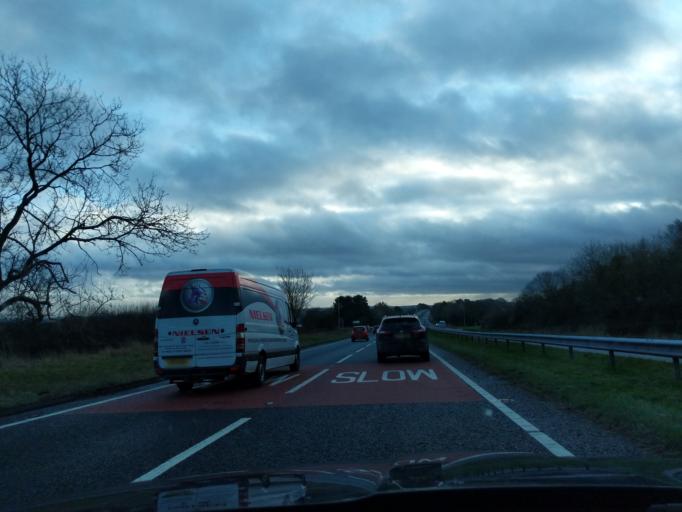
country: GB
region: England
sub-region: Northumberland
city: Felton
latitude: 55.3320
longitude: -1.7250
